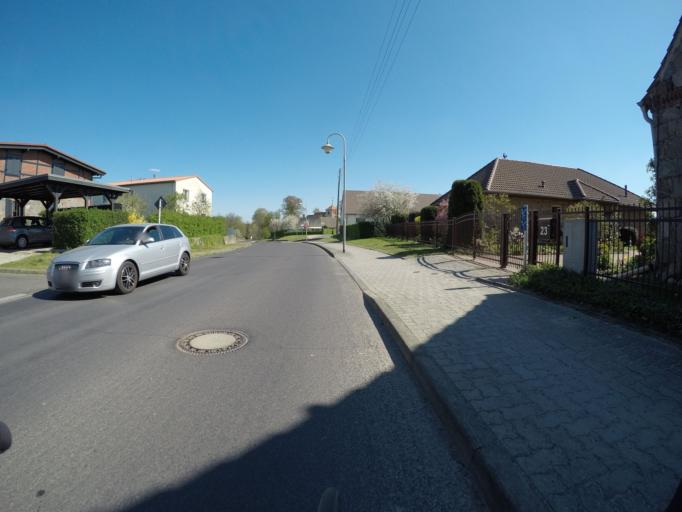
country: DE
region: Brandenburg
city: Strausberg
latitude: 52.6098
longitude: 13.8652
